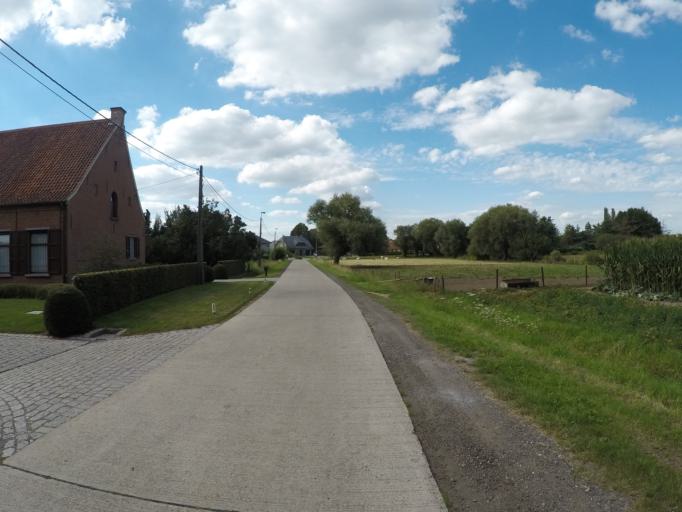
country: BE
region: Flanders
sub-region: Provincie Antwerpen
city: Ranst
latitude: 51.1673
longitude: 4.6115
